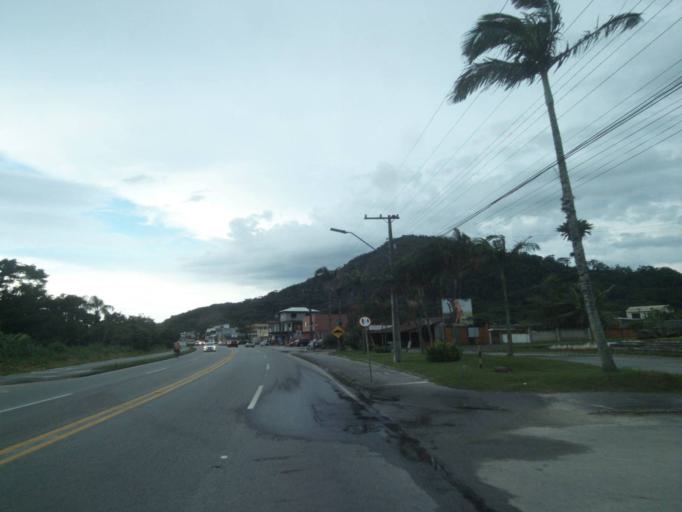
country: BR
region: Parana
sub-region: Guaratuba
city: Guaratuba
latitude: -25.8124
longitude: -48.5509
